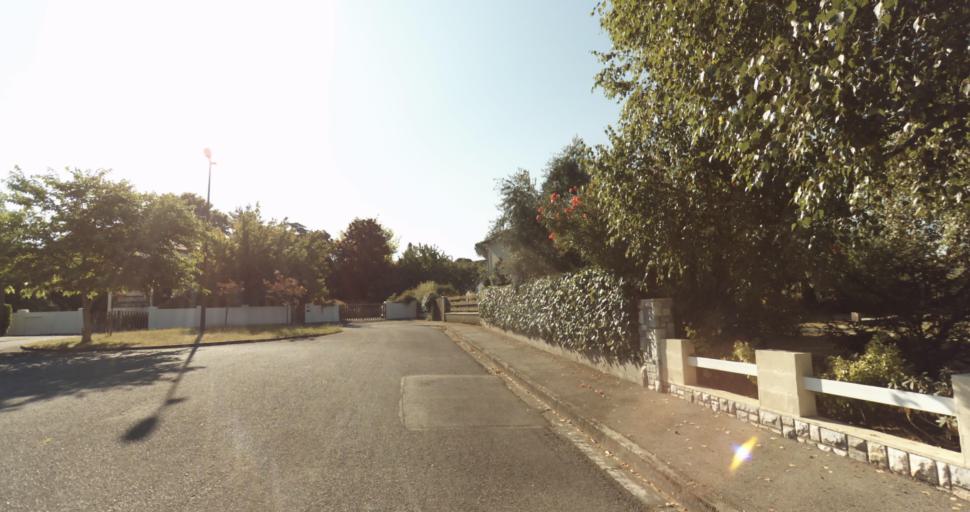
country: FR
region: Midi-Pyrenees
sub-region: Departement de la Haute-Garonne
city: L'Union
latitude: 43.6664
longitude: 1.4824
